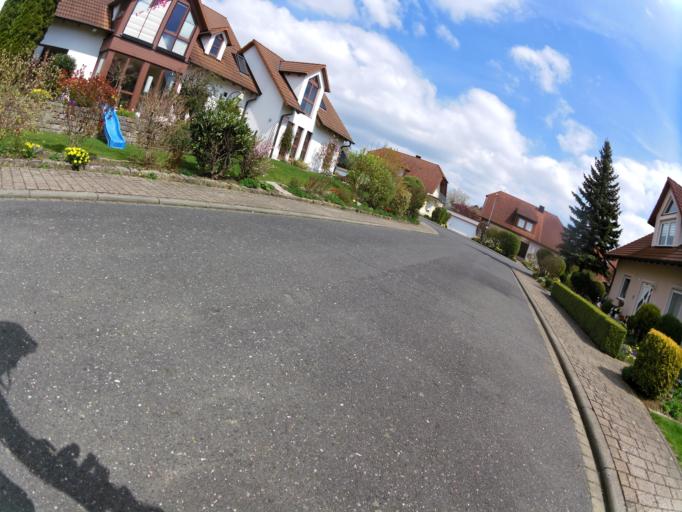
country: DE
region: Bavaria
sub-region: Regierungsbezirk Unterfranken
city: Giebelstadt
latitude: 49.6530
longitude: 9.9367
